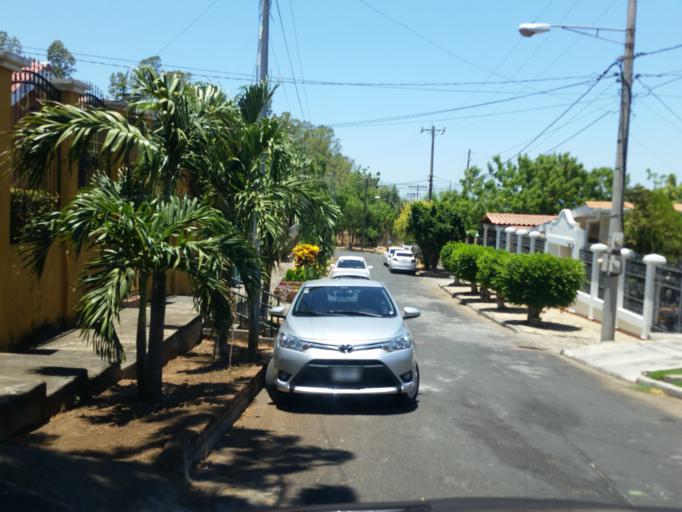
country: NI
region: Managua
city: Managua
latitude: 12.1077
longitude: -86.2466
